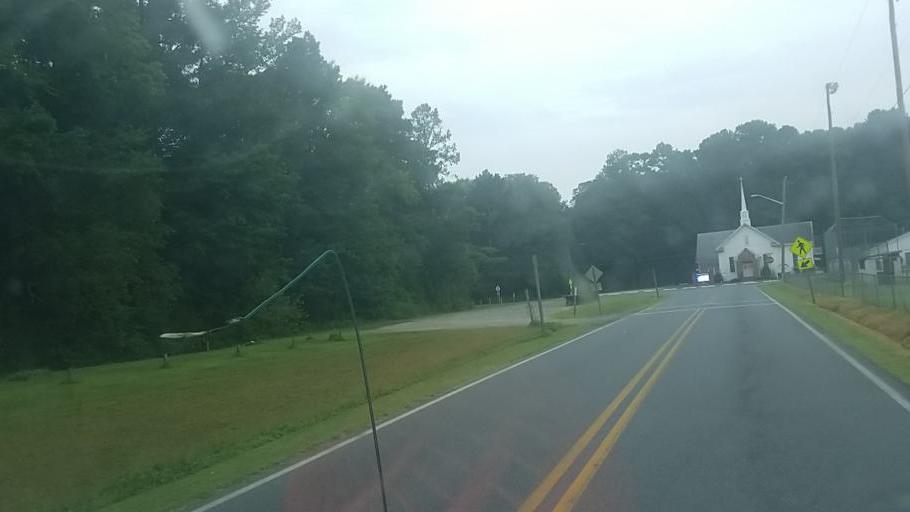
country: US
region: Maryland
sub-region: Wicomico County
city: Delmar
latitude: 38.3995
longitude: -75.5333
